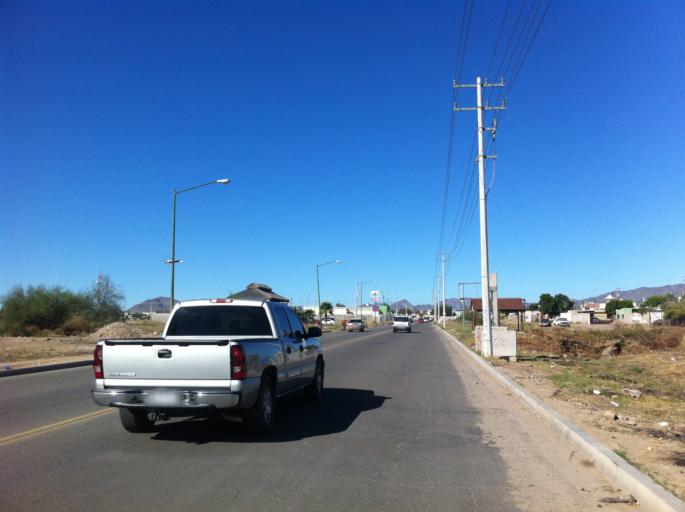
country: MX
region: Sonora
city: Hermosillo
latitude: 29.1127
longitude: -111.0056
